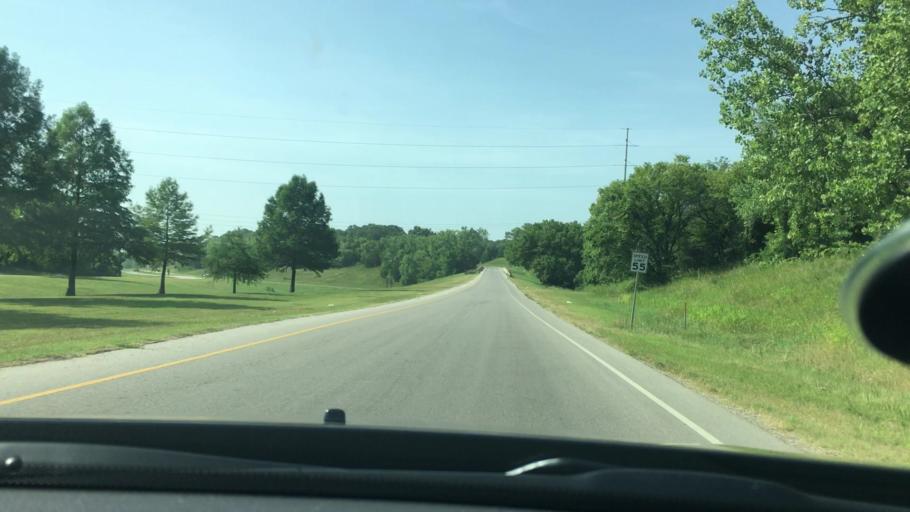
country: US
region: Oklahoma
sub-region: Pontotoc County
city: Ada
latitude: 34.7523
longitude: -96.6577
